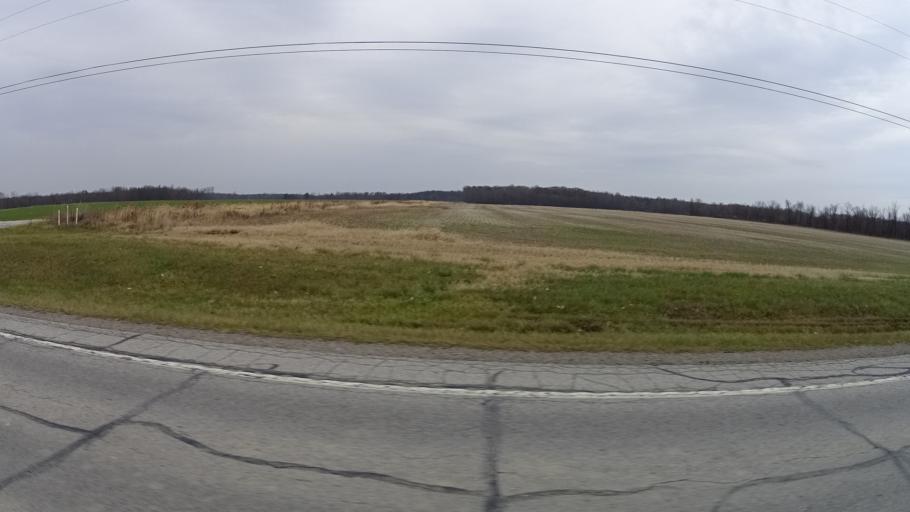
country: US
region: Ohio
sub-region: Lorain County
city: Lagrange
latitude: 41.1681
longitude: -82.0733
